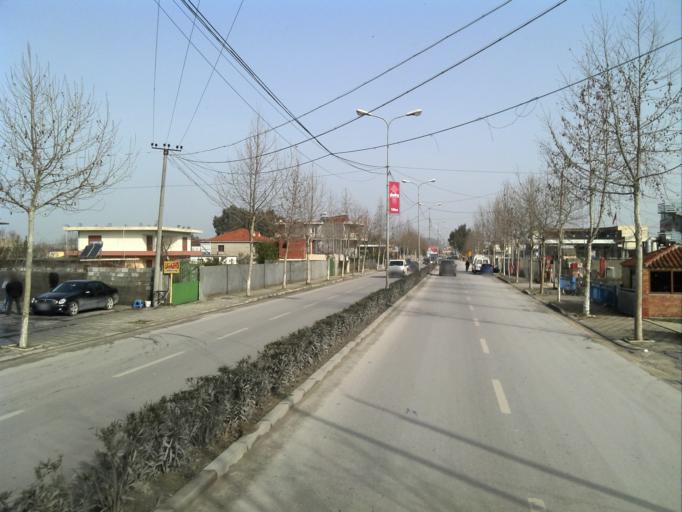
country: AL
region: Fier
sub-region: Rrethi i Fierit
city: Mbrostar-Ure
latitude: 40.7414
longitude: 19.5764
